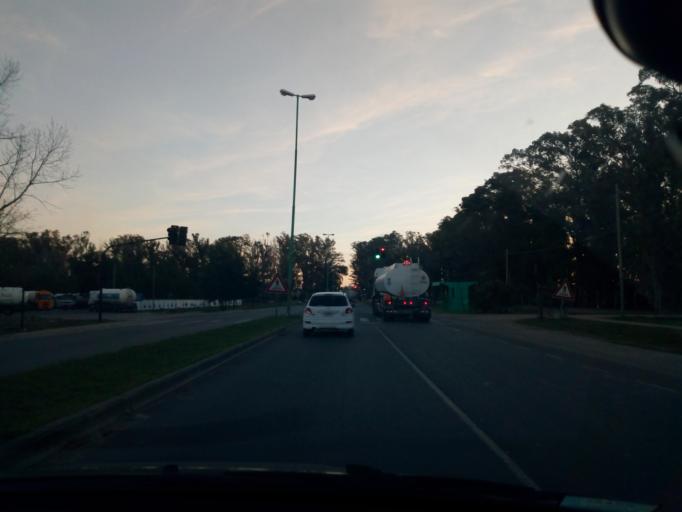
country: AR
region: Buenos Aires
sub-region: Partido de La Plata
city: La Plata
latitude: -34.8918
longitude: -57.9365
